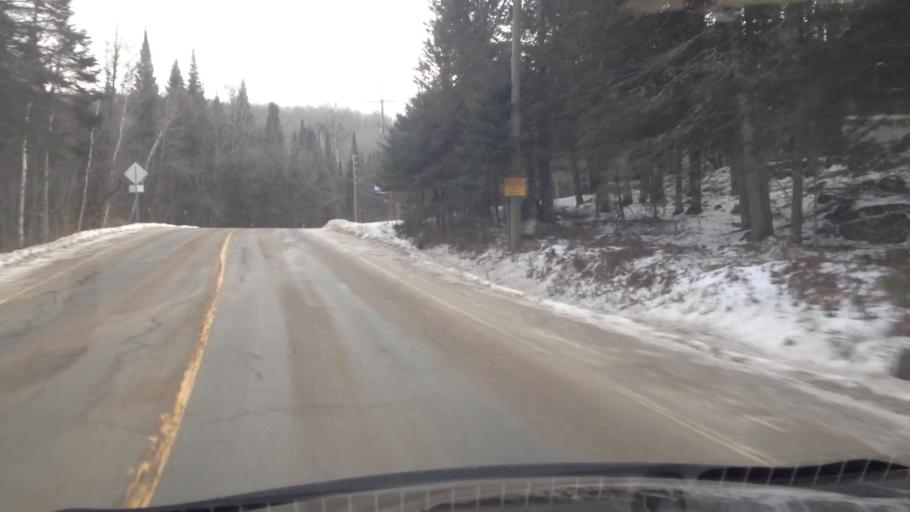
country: CA
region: Quebec
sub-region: Laurentides
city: Mont-Tremblant
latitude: 45.9359
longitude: -74.5437
